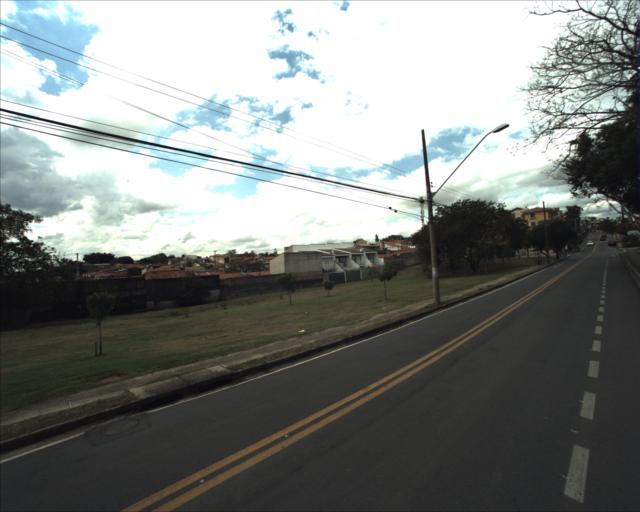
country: BR
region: Sao Paulo
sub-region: Sorocaba
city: Sorocaba
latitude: -23.5219
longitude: -47.4773
